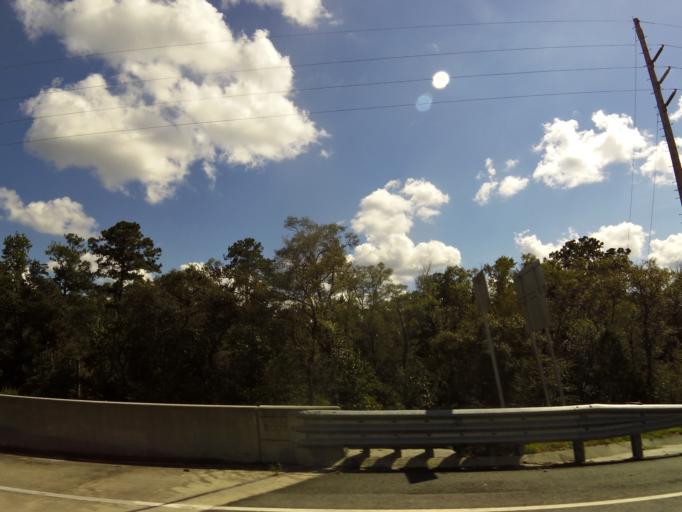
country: US
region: Georgia
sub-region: Clinch County
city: Homerville
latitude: 30.6828
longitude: -82.5840
